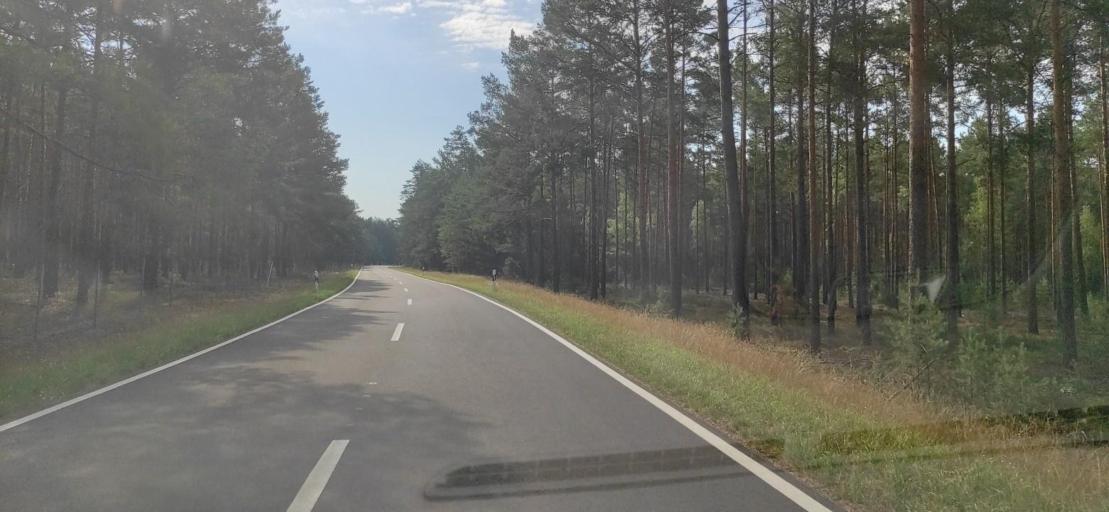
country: PL
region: Lubusz
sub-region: Powiat zarski
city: Trzebiel
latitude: 51.6638
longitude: 14.7373
